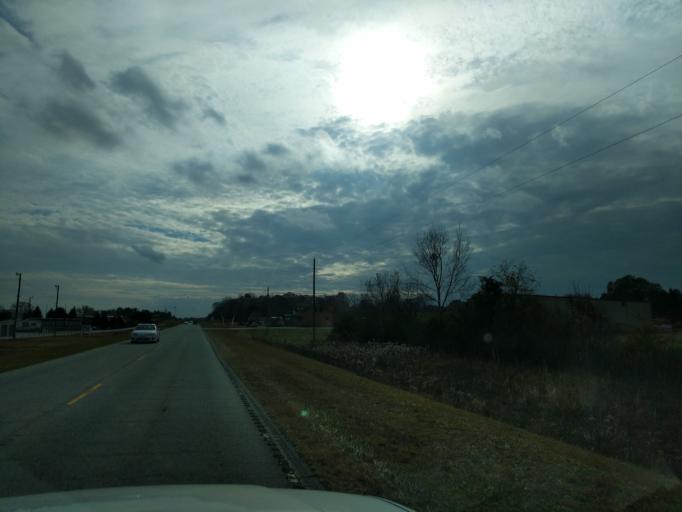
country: US
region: Georgia
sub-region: Franklin County
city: Gumlog
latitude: 34.5426
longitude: -83.0511
